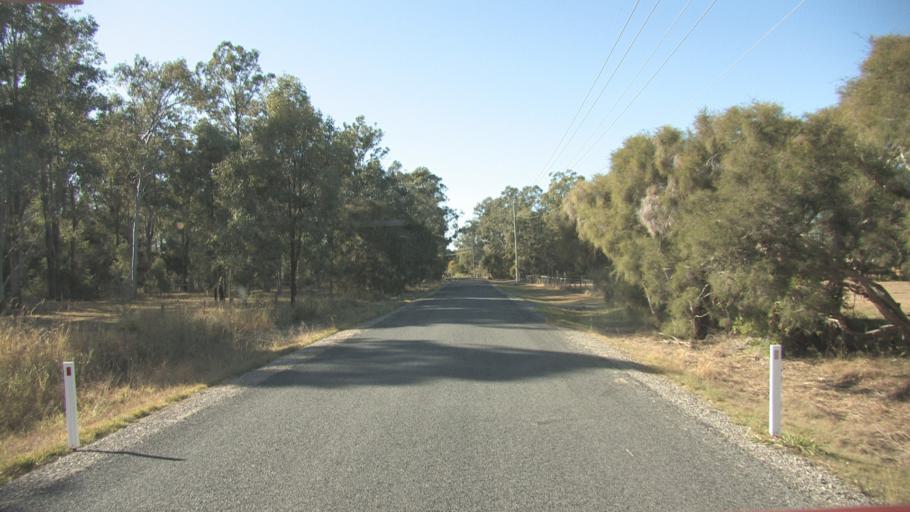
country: AU
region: Queensland
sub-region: Logan
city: Cedar Vale
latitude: -27.8422
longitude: 152.9991
